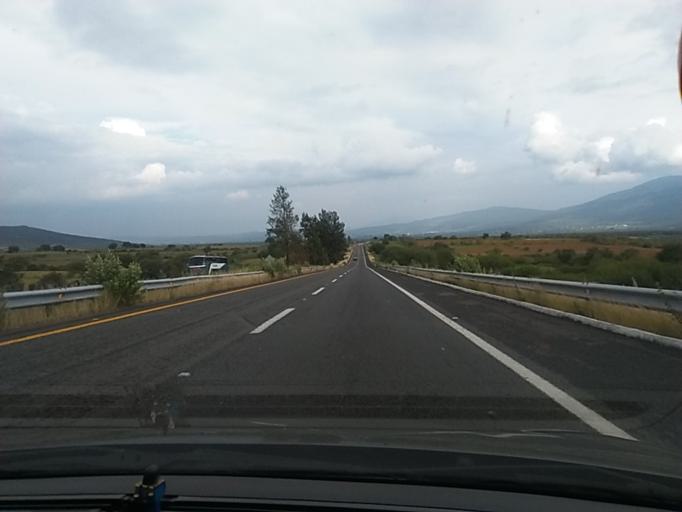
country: MX
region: Michoacan
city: Ixtlan
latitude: 20.1855
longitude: -102.3052
